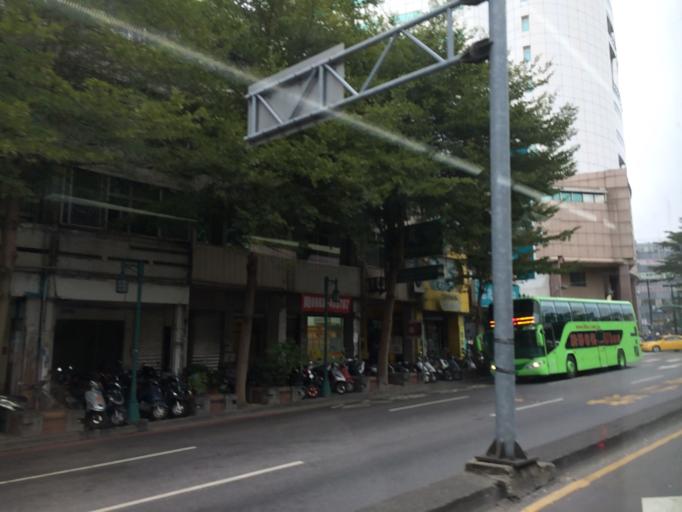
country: TW
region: Taiwan
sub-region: Taichung City
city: Taichung
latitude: 24.1361
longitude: 120.6827
